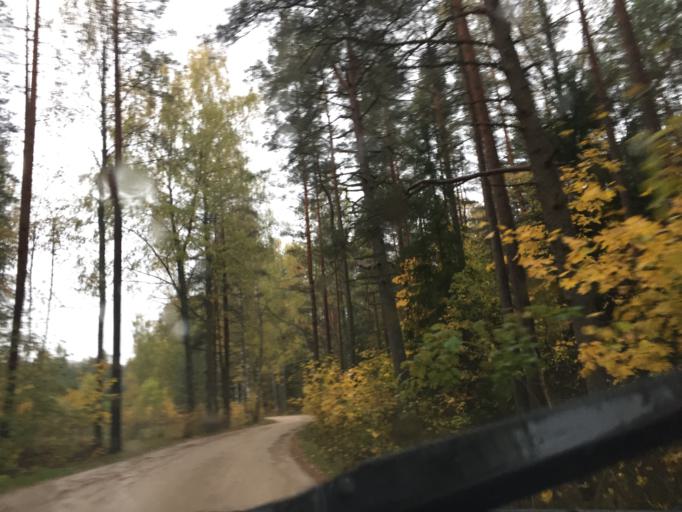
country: LV
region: Engure
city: Smarde
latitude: 56.9249
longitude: 23.4721
